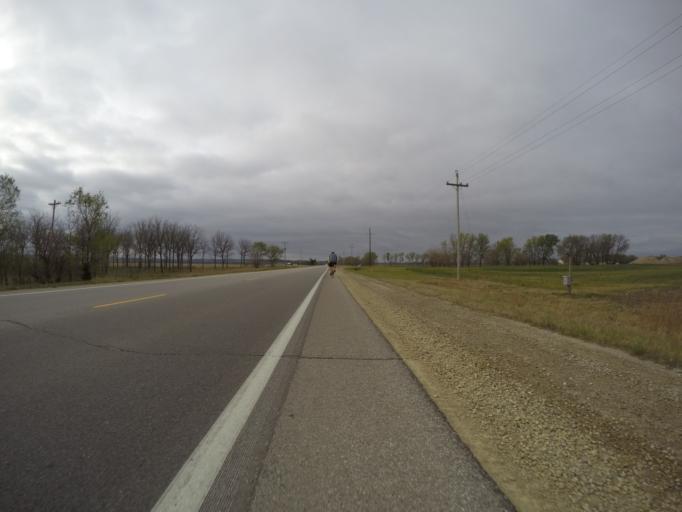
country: US
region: Kansas
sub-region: Pottawatomie County
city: Wamego
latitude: 39.1787
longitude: -96.3054
